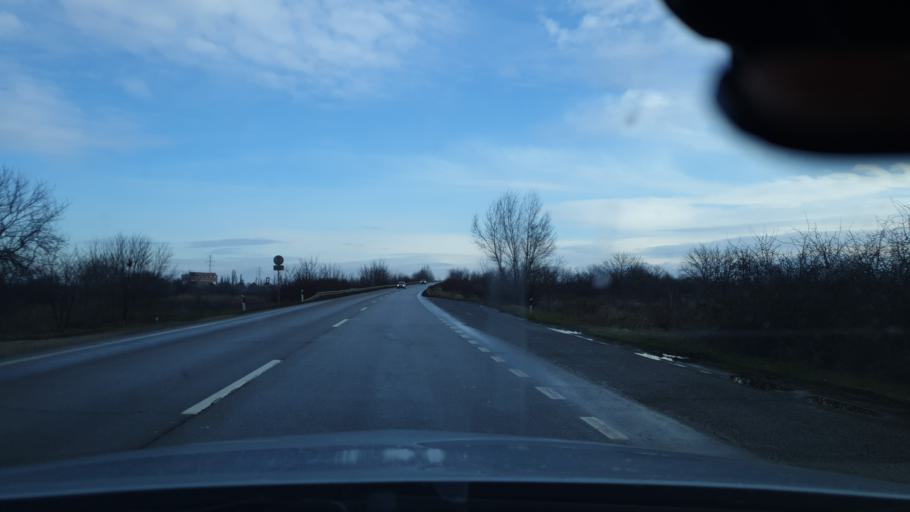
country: RS
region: Central Serbia
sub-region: Podunavski Okrug
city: Smederevo
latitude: 44.5844
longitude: 20.9901
